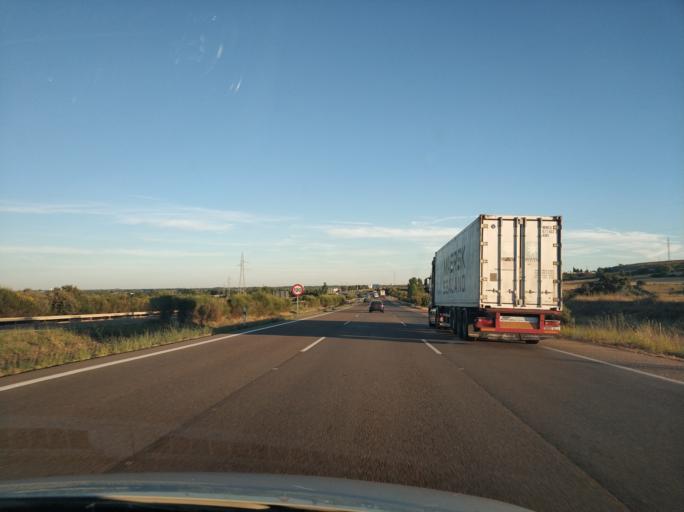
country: ES
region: Castille and Leon
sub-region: Provincia de Zamora
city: Benavente
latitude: 42.0280
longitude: -5.6711
